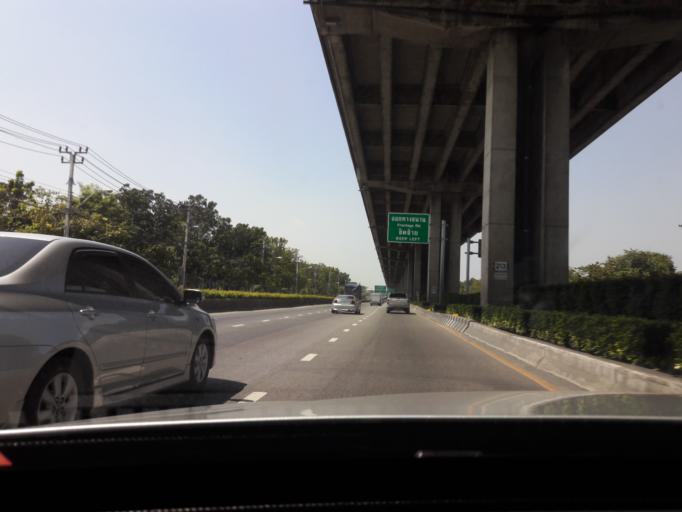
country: TH
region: Bangkok
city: Thawi Watthana
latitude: 13.7844
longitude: 100.3941
